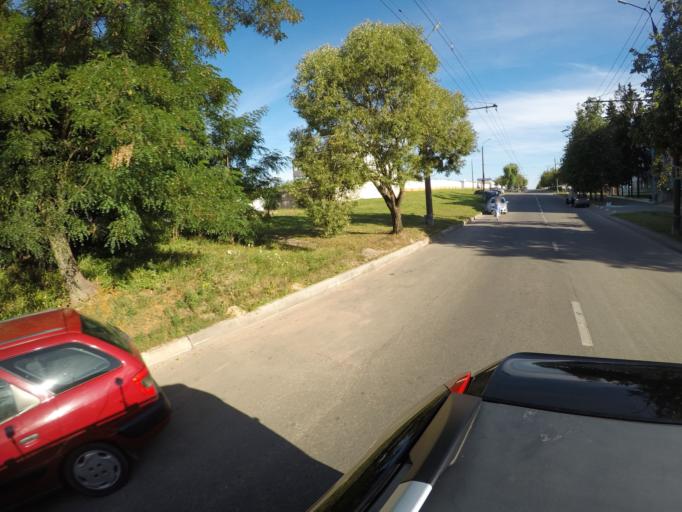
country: BY
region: Grodnenskaya
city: Hrodna
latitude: 53.7124
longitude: 23.8262
